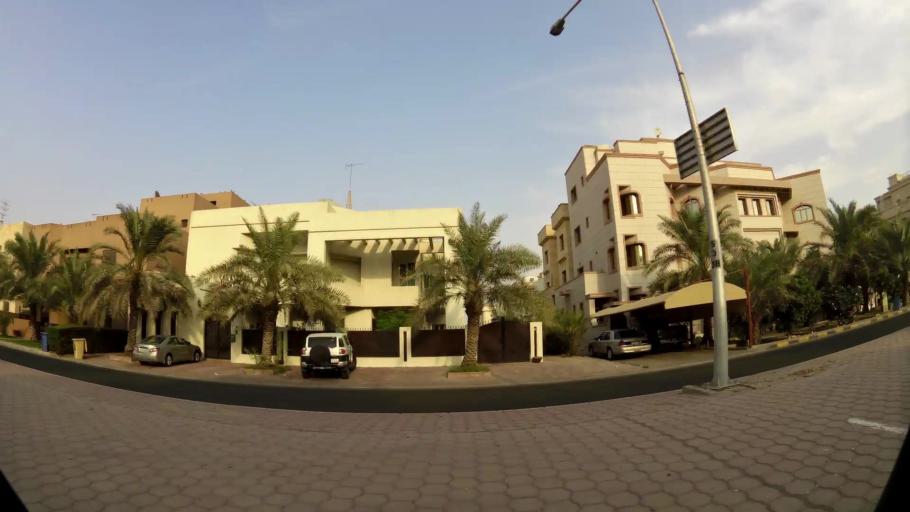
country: KW
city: Bayan
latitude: 29.3104
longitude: 48.0331
